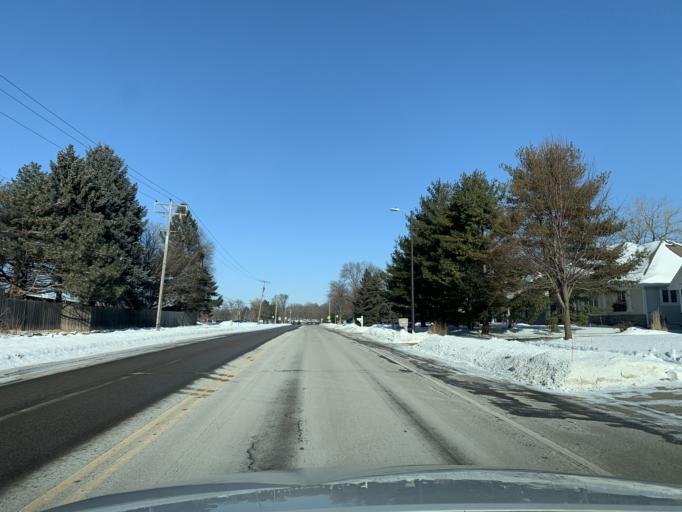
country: US
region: Minnesota
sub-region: Scott County
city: Savage
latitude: 44.8300
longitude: -93.3584
